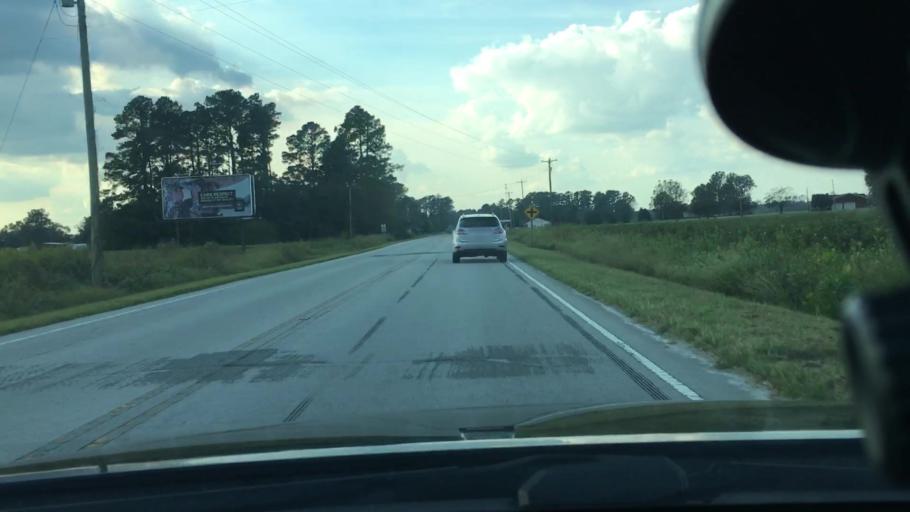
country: US
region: North Carolina
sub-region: Craven County
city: Vanceboro
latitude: 35.3763
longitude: -77.2144
